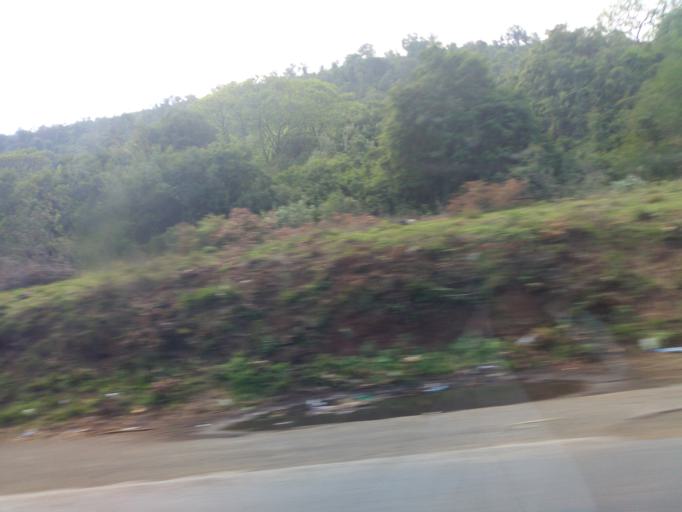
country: KE
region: Kiambu
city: Limuru
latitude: -1.0219
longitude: 36.6035
